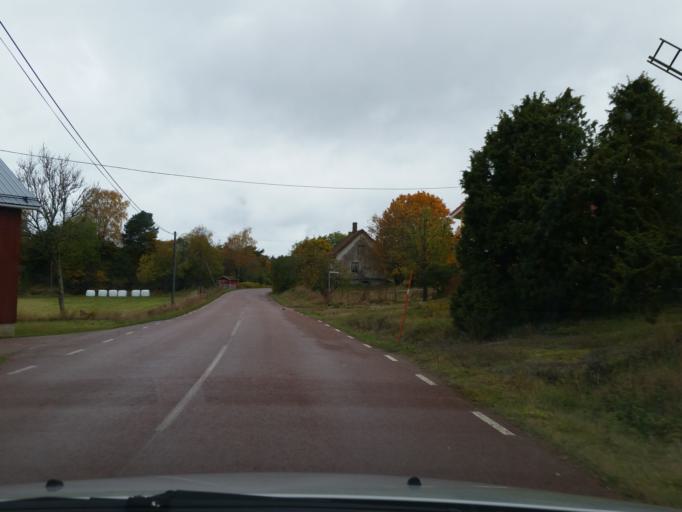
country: AX
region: Alands landsbygd
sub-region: Lumparland
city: Lumparland
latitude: 60.1212
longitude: 20.2470
